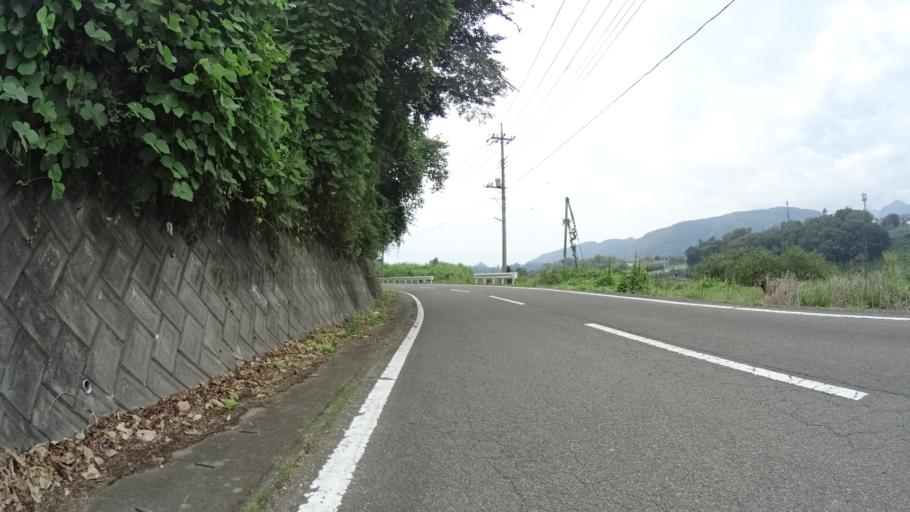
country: JP
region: Yamanashi
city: Enzan
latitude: 35.7468
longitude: 138.7229
